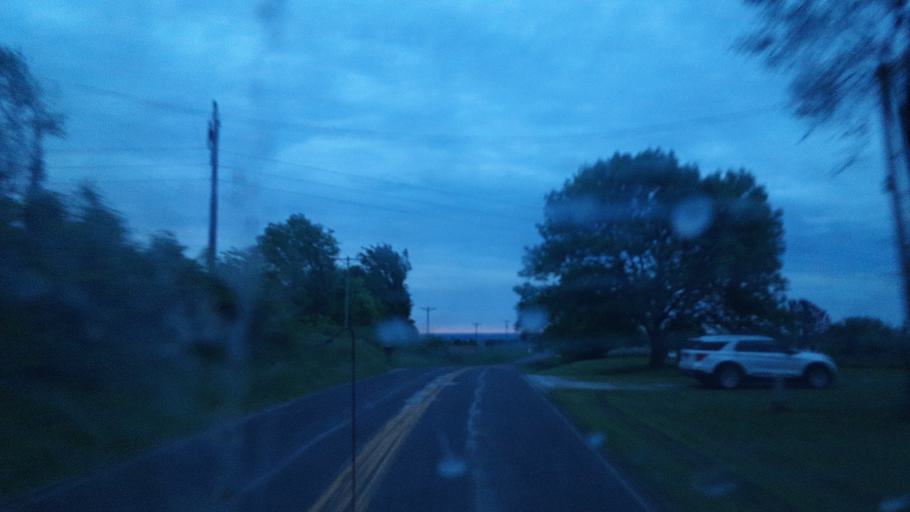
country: US
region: Missouri
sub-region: Clark County
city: Kahoka
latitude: 40.4339
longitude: -91.5859
